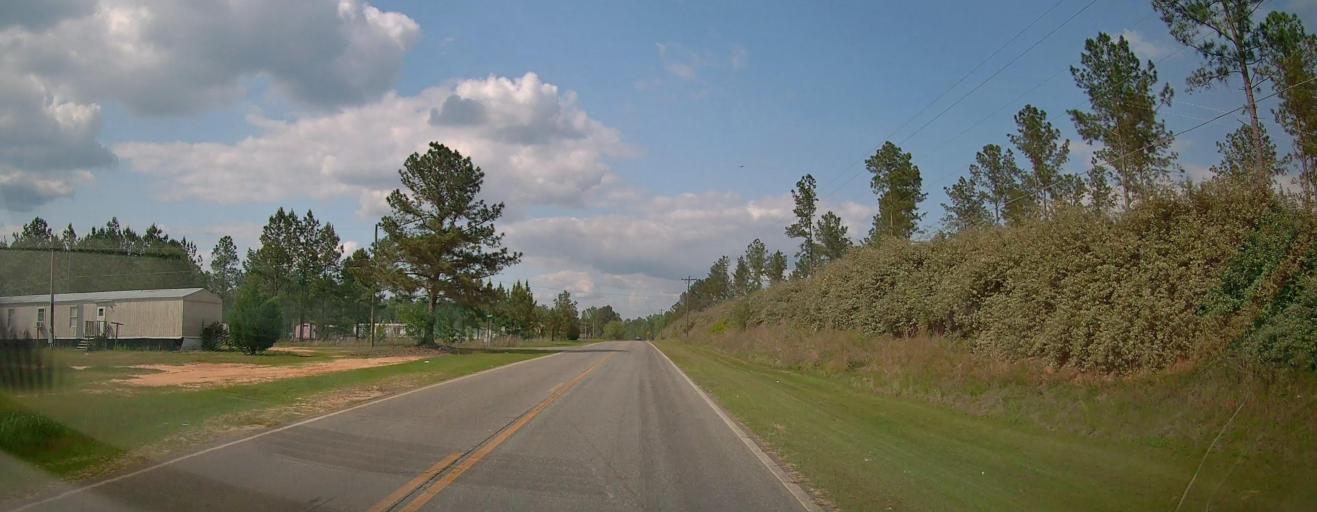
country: US
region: Georgia
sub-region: Laurens County
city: East Dublin
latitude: 32.5756
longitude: -82.8645
